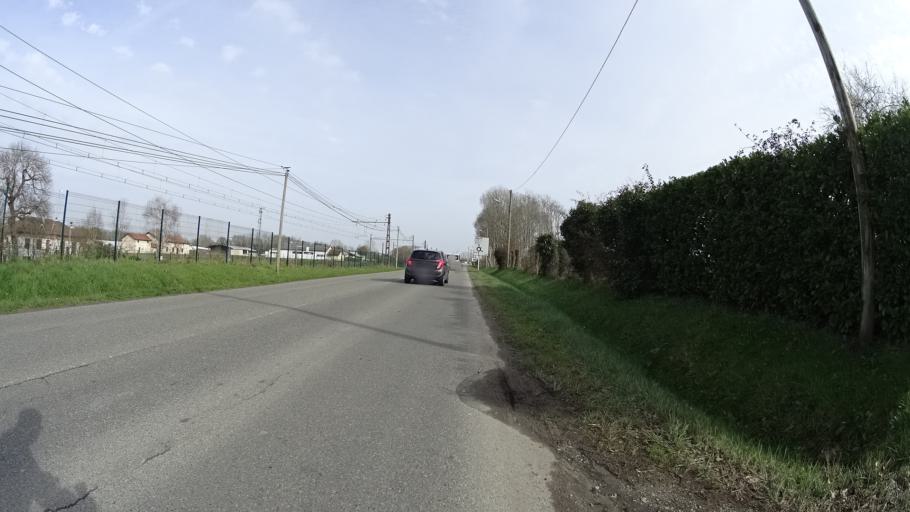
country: FR
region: Aquitaine
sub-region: Departement des Landes
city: Dax
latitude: 43.6947
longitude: -1.0368
